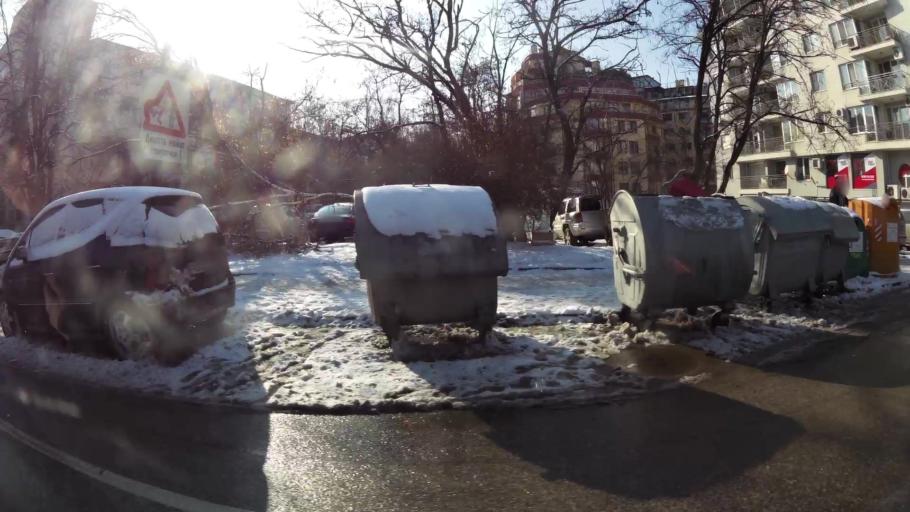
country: BG
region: Sofia-Capital
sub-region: Stolichna Obshtina
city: Sofia
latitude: 42.6636
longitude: 23.3442
